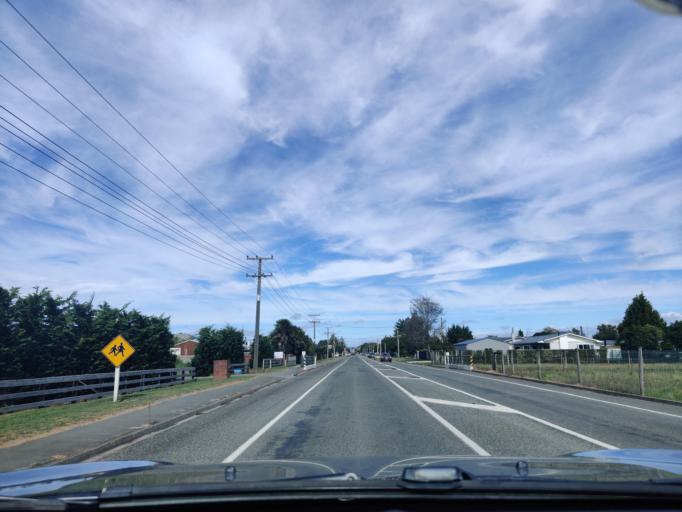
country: NZ
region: Tasman
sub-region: Tasman District
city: Richmond
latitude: -41.3520
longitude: 173.1573
